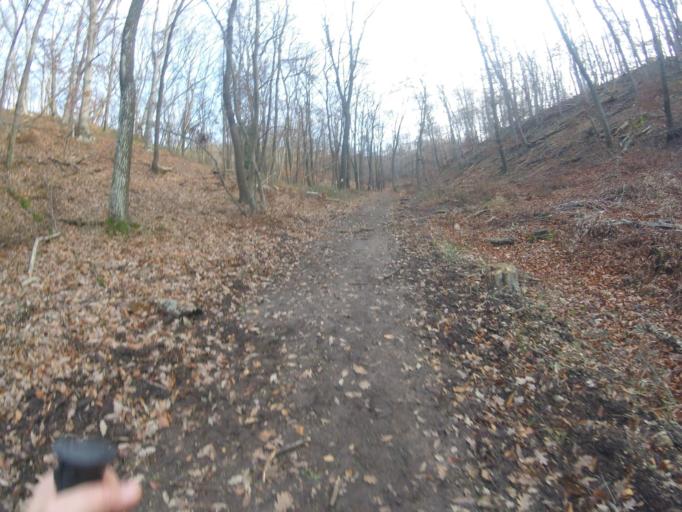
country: HU
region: Veszprem
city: Sumeg
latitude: 46.9135
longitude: 17.3447
